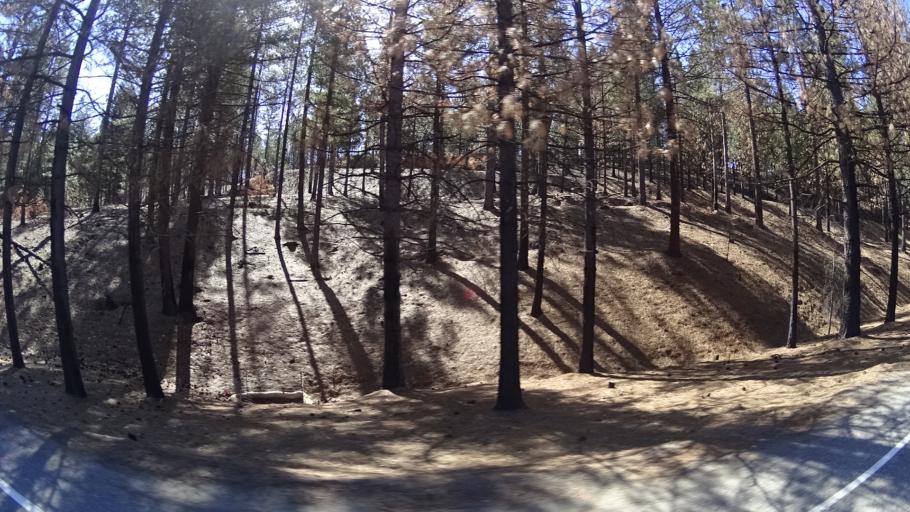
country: US
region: California
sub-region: Tehama County
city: Rancho Tehama Reserve
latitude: 39.6507
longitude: -122.7377
